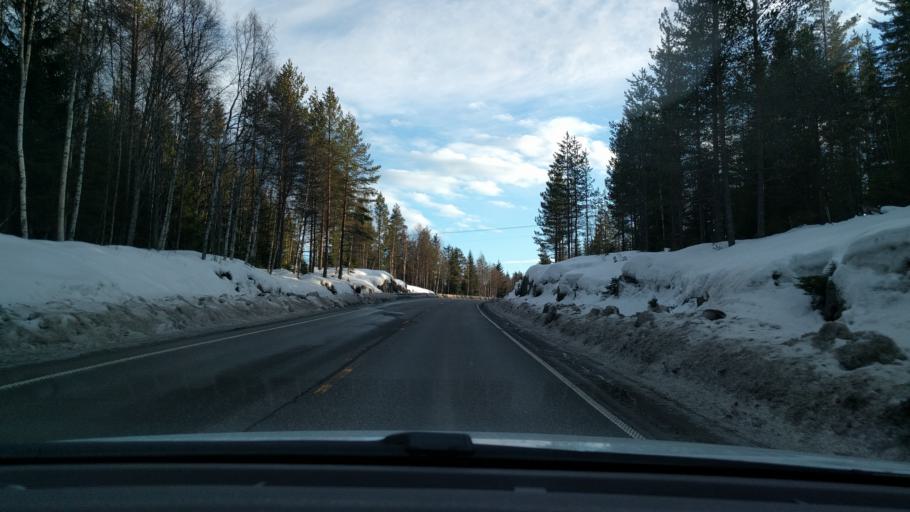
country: NO
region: Hedmark
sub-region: Elverum
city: Elverum
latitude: 61.0228
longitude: 11.8616
